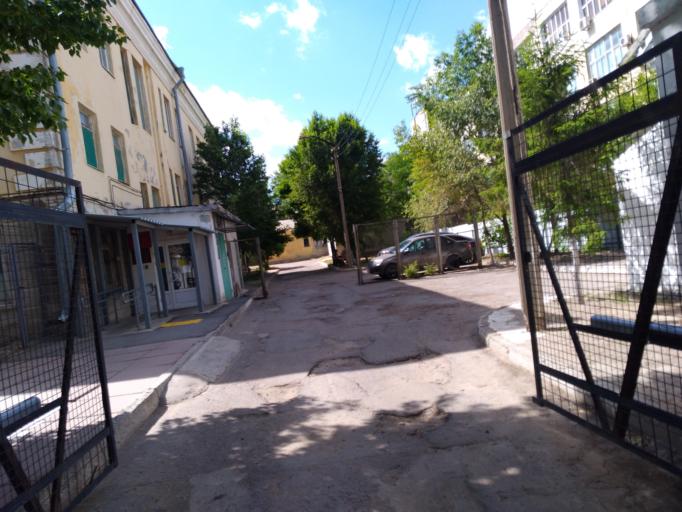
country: RU
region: Volgograd
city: Volgograd
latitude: 48.7198
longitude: 44.5357
